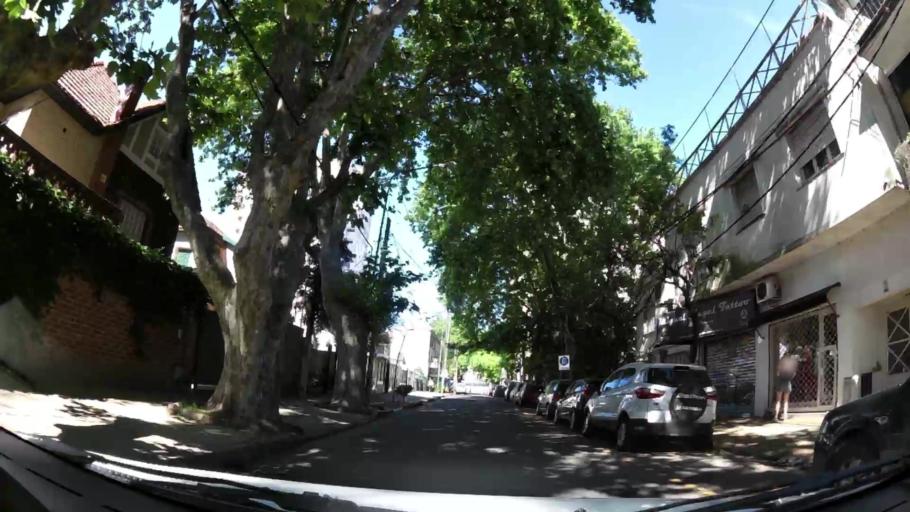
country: AR
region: Buenos Aires
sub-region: Partido de Vicente Lopez
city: Olivos
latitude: -34.5261
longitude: -58.4810
